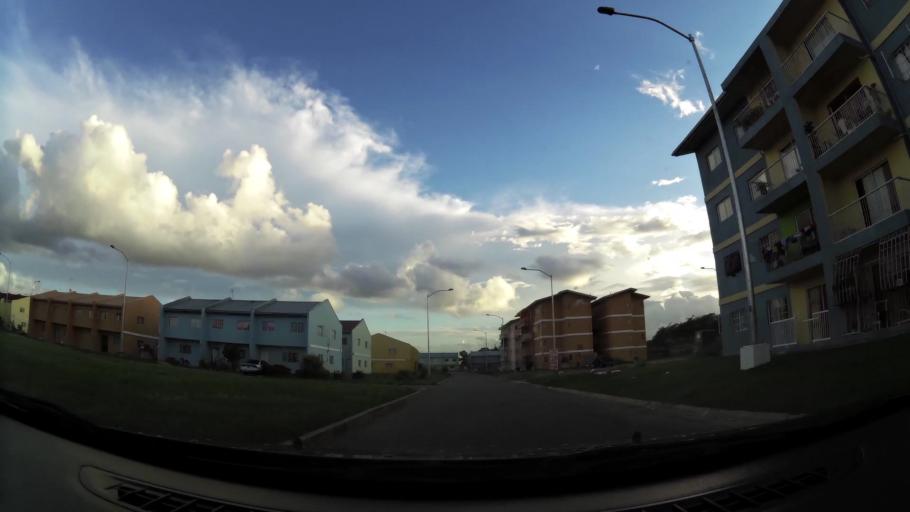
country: TT
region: Tunapuna/Piarco
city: Arouca
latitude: 10.6128
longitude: -61.3561
